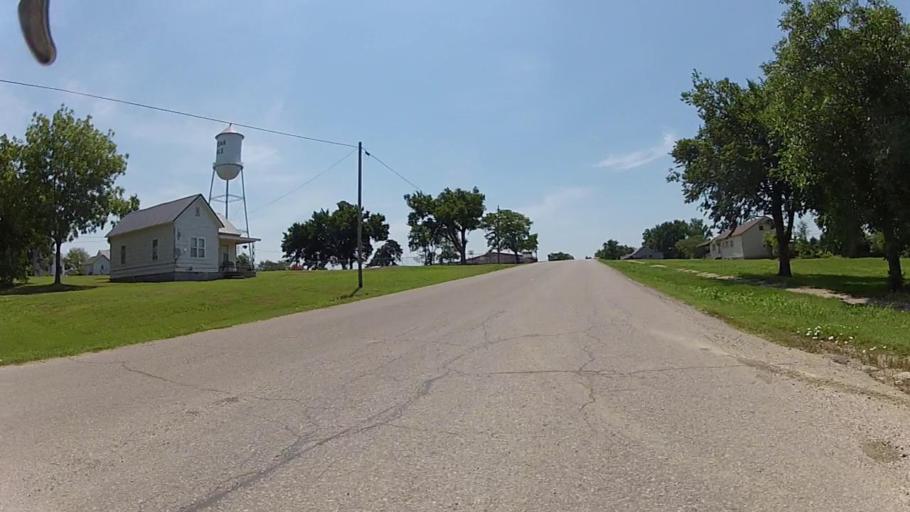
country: US
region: Kansas
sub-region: Chautauqua County
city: Sedan
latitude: 37.1072
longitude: -96.5028
